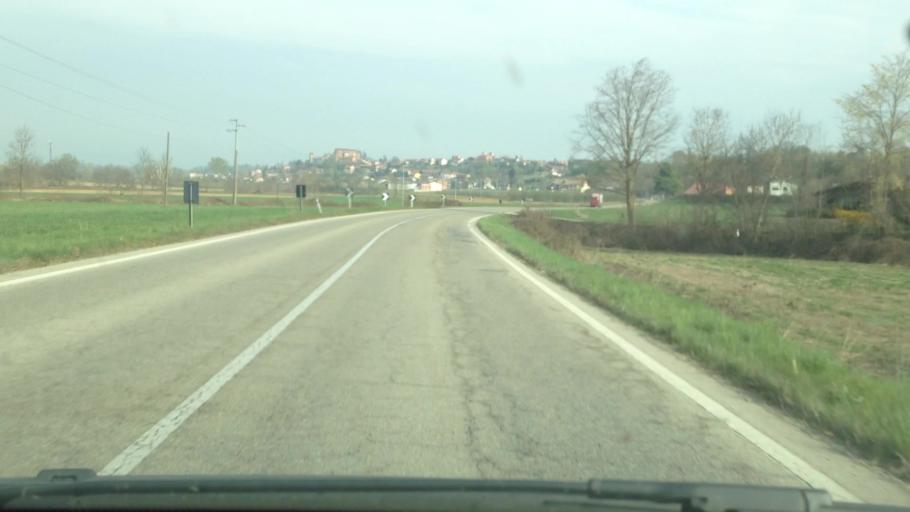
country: IT
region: Piedmont
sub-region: Provincia di Torino
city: Pralormo
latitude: 44.8470
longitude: 7.9096
